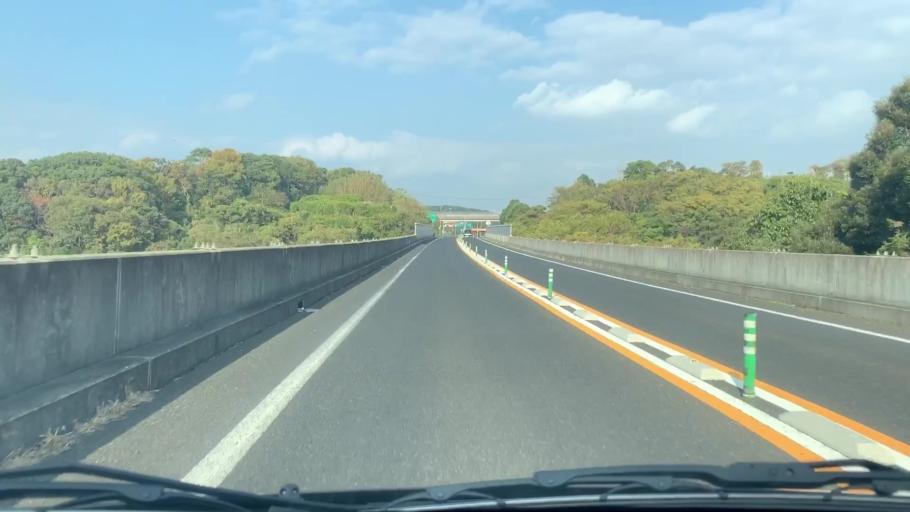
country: JP
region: Nagasaki
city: Sasebo
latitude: 33.0615
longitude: 129.7595
